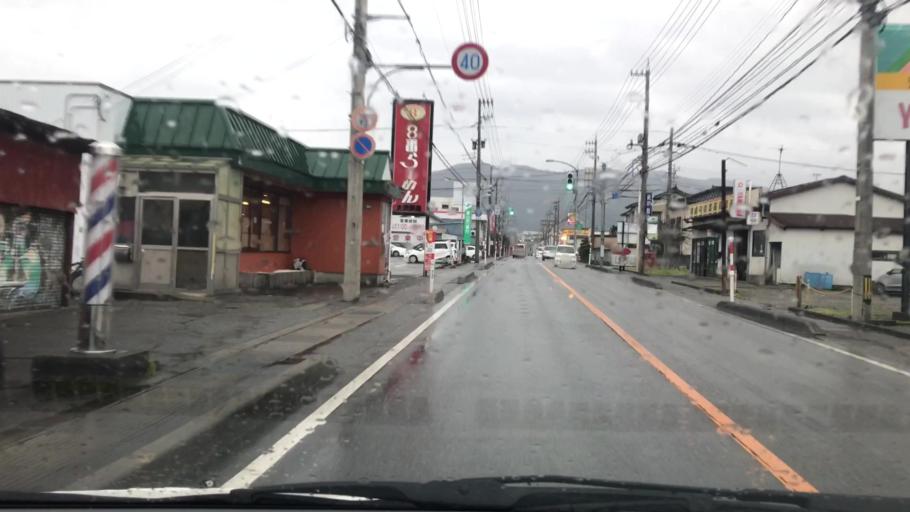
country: JP
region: Toyama
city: Yatsuomachi-higashikumisaka
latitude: 36.5839
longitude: 137.2062
